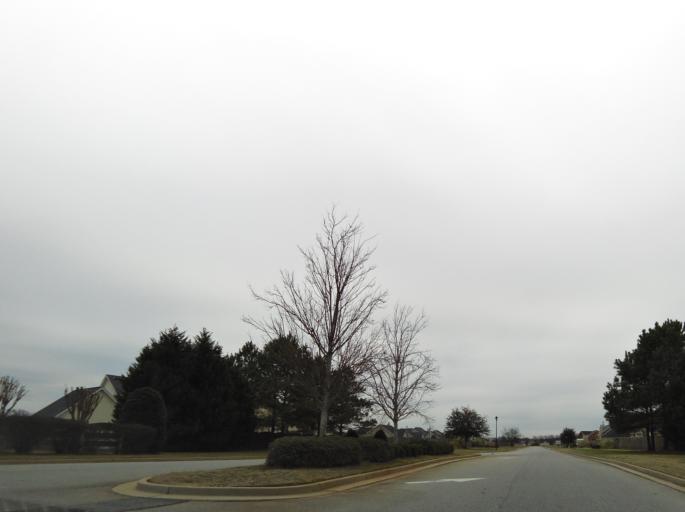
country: US
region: Georgia
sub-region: Houston County
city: Centerville
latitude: 32.7140
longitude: -83.6923
